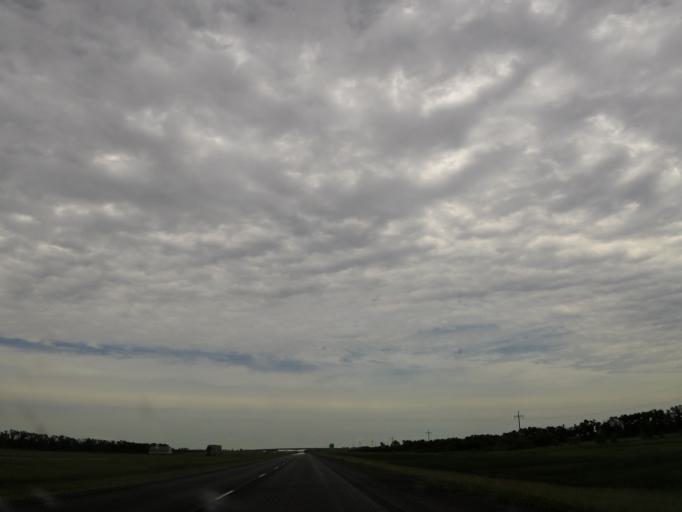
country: US
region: North Dakota
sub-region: Walsh County
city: Grafton
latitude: 48.2868
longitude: -97.1888
